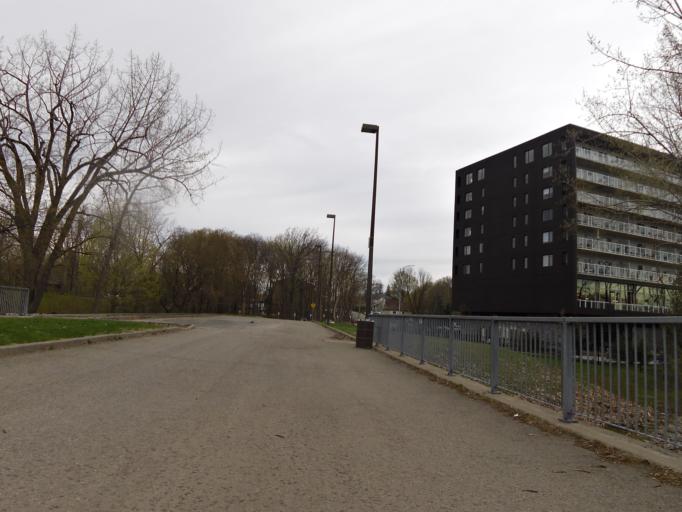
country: CA
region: Quebec
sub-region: Laurentides
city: Deux-Montagnes
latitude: 45.5345
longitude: -73.8836
